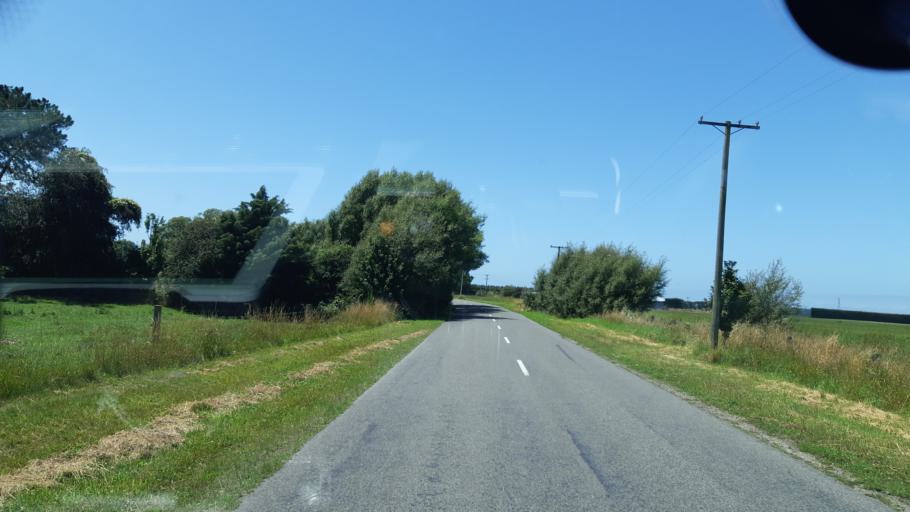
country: NZ
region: Canterbury
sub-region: Waimakariri District
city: Woodend
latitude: -43.2839
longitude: 172.6385
